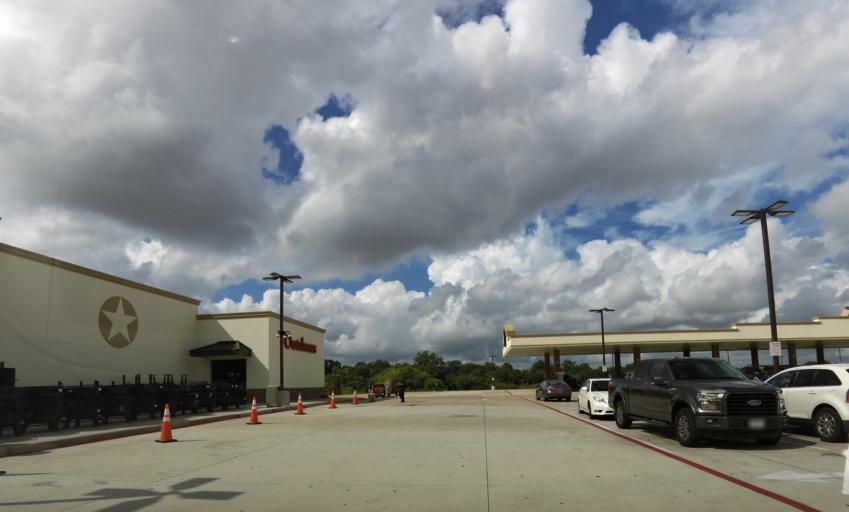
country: US
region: Texas
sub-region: Caldwell County
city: Luling
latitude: 29.6511
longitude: -97.5931
